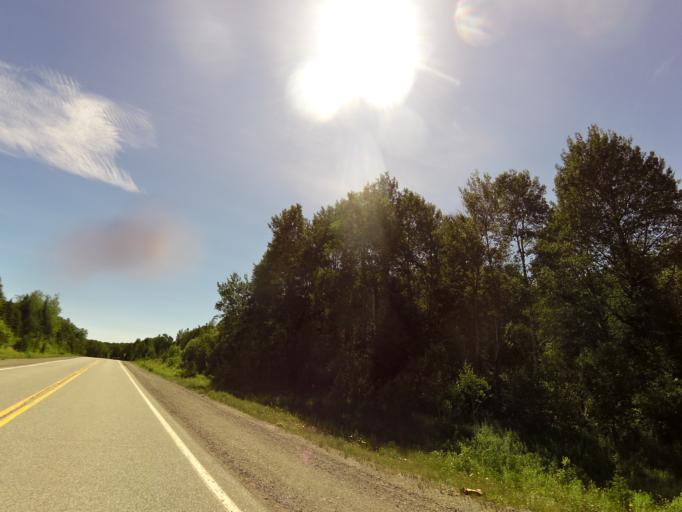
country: CA
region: Quebec
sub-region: Nord-du-Quebec
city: Lebel-sur-Quevillon
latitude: 48.8673
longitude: -77.1402
